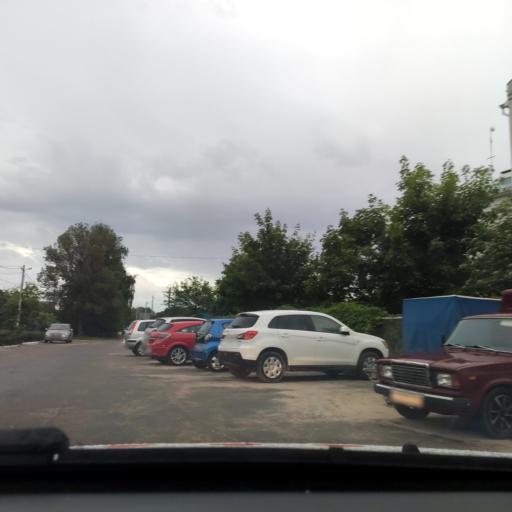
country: RU
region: Voronezj
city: Podgornoye
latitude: 51.7919
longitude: 39.1503
